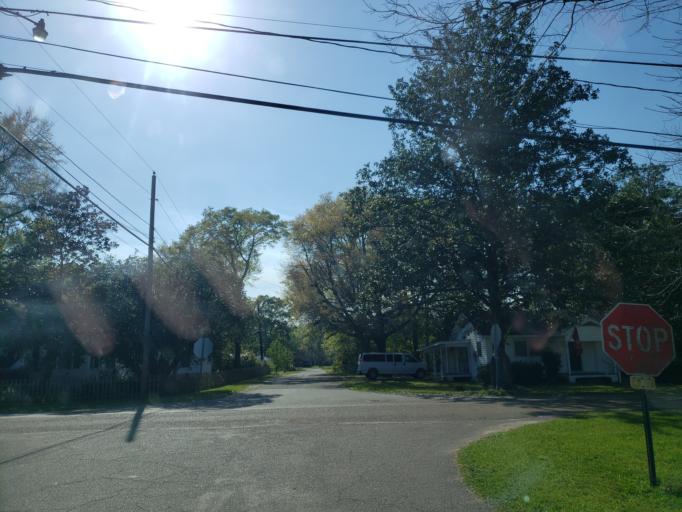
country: US
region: Mississippi
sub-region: Perry County
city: New Augusta
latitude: 31.1677
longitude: -88.9207
